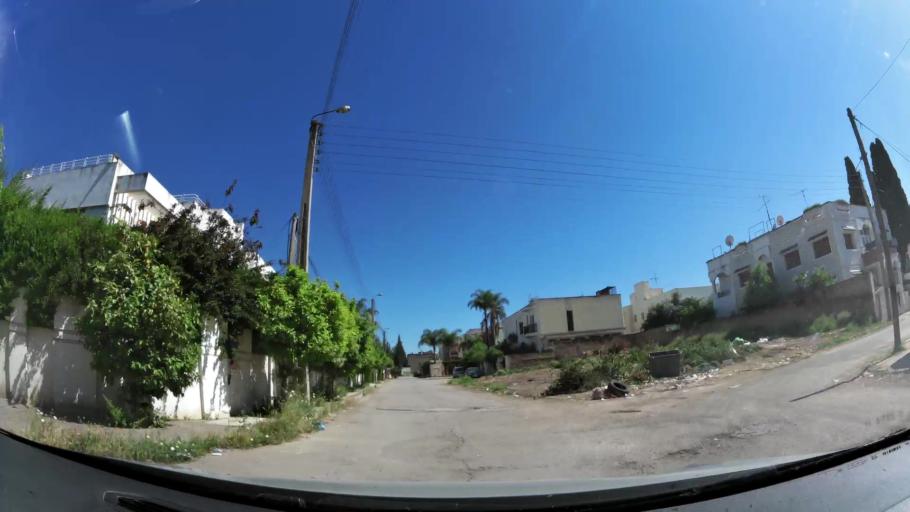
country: MA
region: Fes-Boulemane
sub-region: Fes
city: Fes
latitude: 34.0174
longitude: -4.9954
